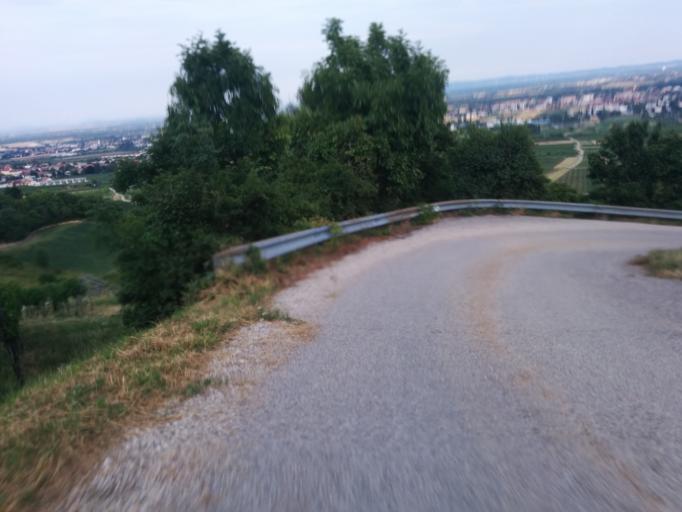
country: AT
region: Lower Austria
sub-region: Politischer Bezirk Modling
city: Gumpoldskirchen
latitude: 48.0401
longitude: 16.2608
